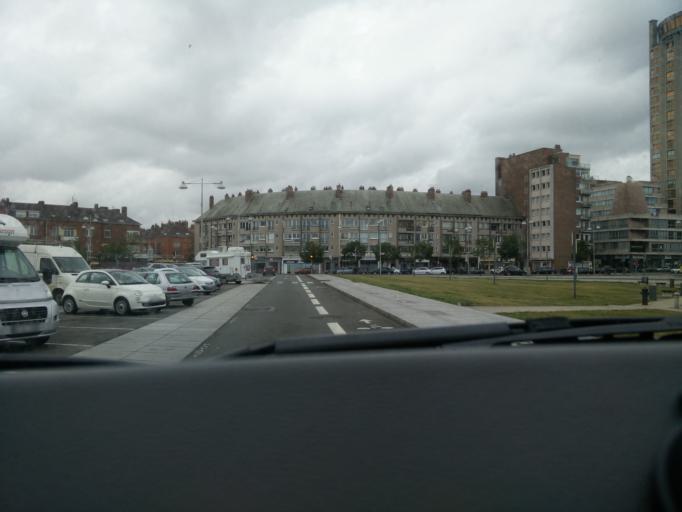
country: FR
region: Nord-Pas-de-Calais
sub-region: Departement du Nord
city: Dunkerque
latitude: 51.0398
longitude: 2.3768
